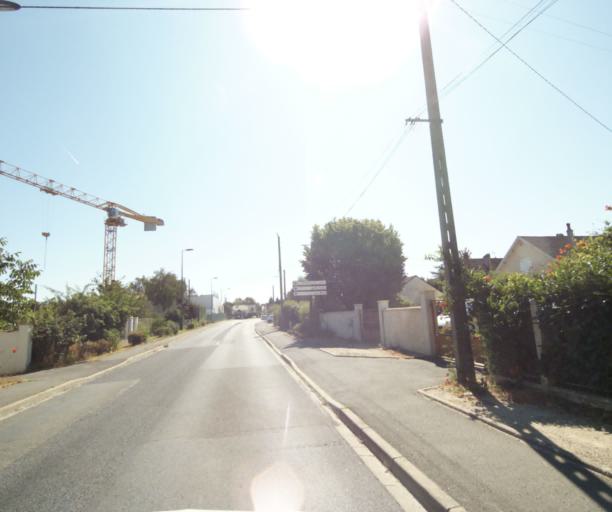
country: FR
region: Ile-de-France
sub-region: Departement de l'Essonne
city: Itteville
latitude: 48.5111
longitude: 2.3422
